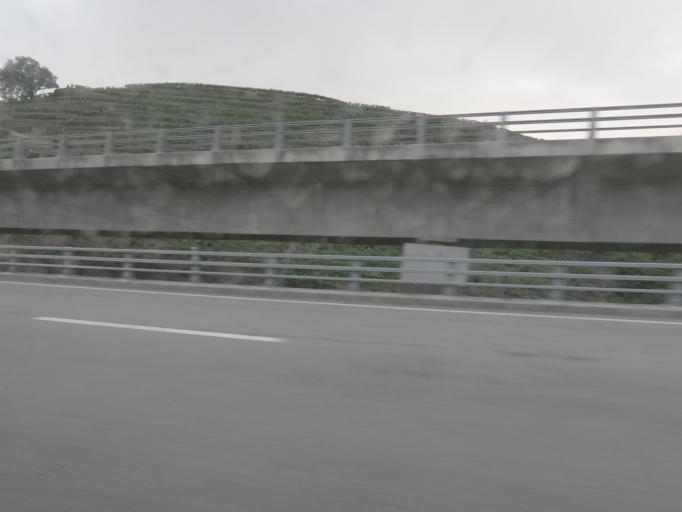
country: PT
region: Vila Real
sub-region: Peso da Regua
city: Peso da Regua
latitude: 41.1866
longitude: -7.7485
